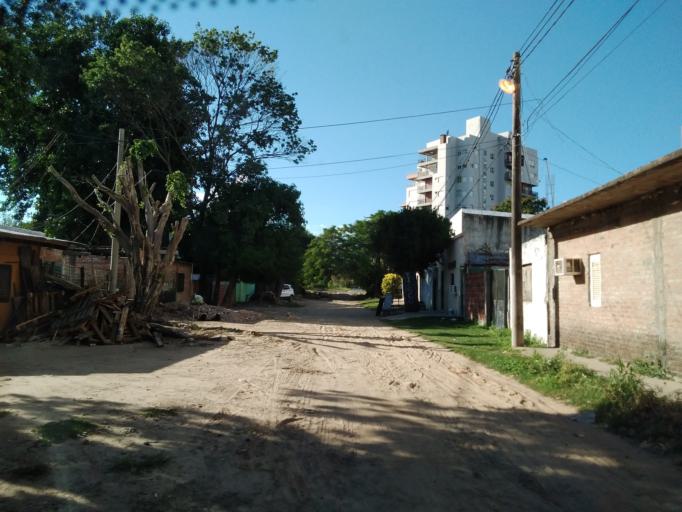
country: AR
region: Corrientes
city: Corrientes
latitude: -27.4770
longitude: -58.8537
